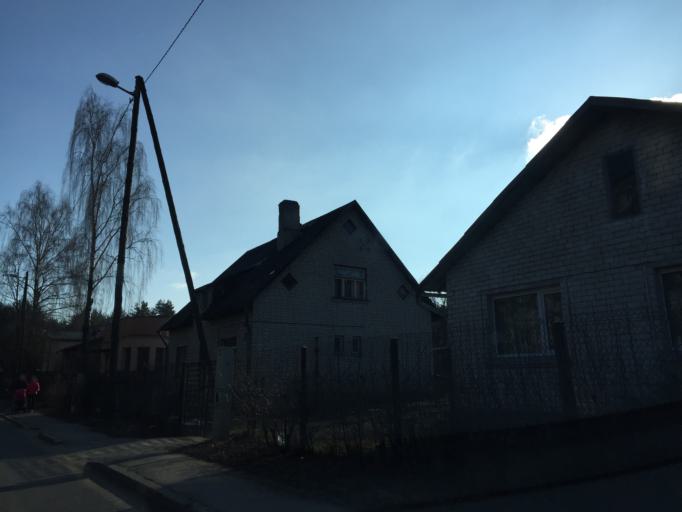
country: LV
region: Riga
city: Bergi
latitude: 56.9755
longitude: 24.2453
